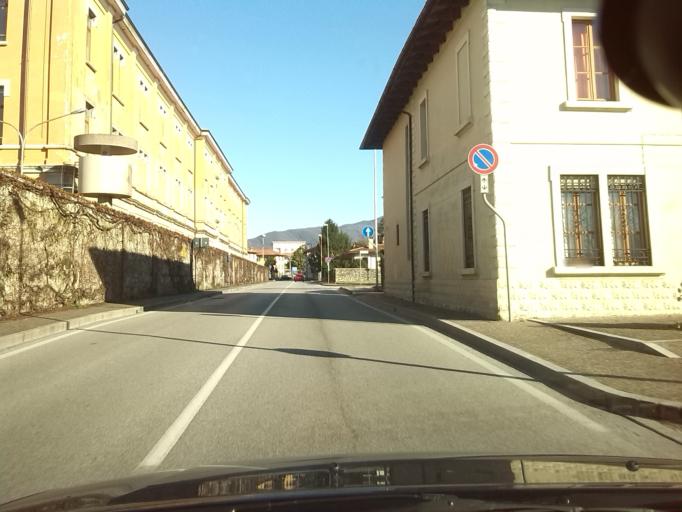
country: IT
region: Friuli Venezia Giulia
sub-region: Provincia di Udine
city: Cividale del Friuli
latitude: 46.0910
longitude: 13.4258
